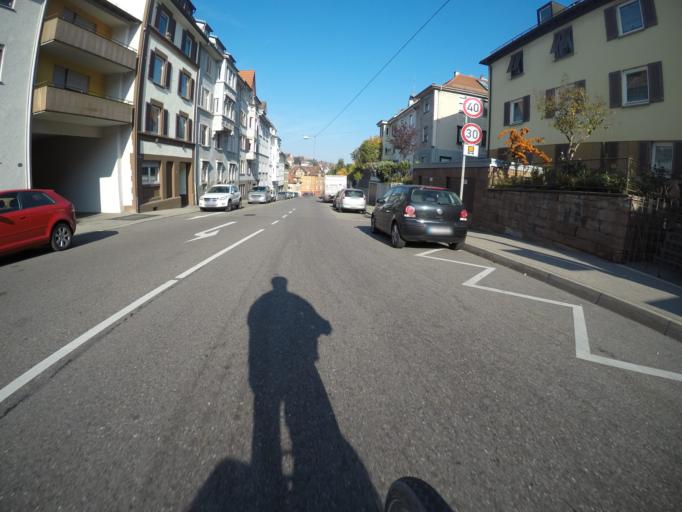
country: DE
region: Baden-Wuerttemberg
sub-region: Regierungsbezirk Stuttgart
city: Stuttgart-Ost
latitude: 48.7720
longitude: 9.2042
